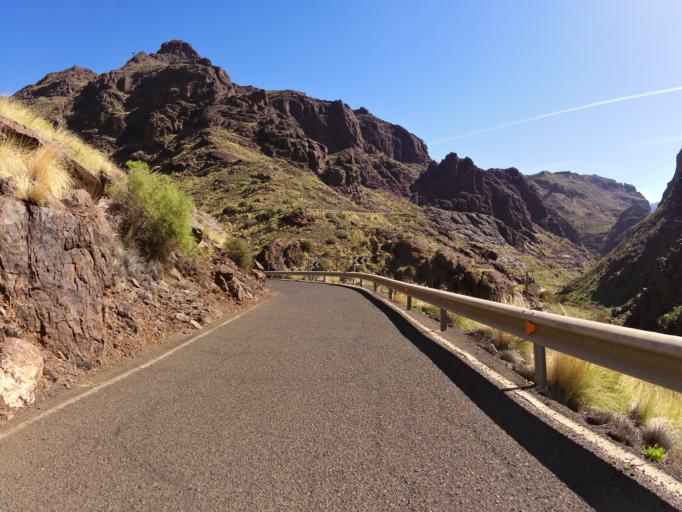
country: ES
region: Canary Islands
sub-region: Provincia de Las Palmas
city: San Nicolas
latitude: 27.9883
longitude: -15.7509
